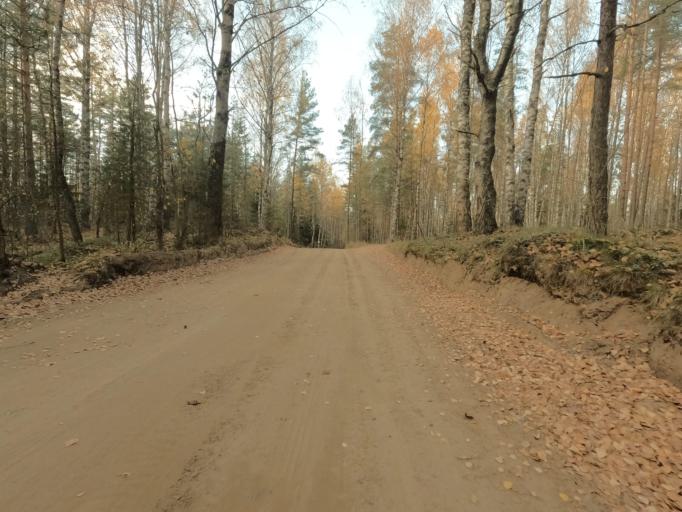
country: RU
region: Leningrad
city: Priladozhskiy
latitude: 59.7405
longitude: 31.3148
